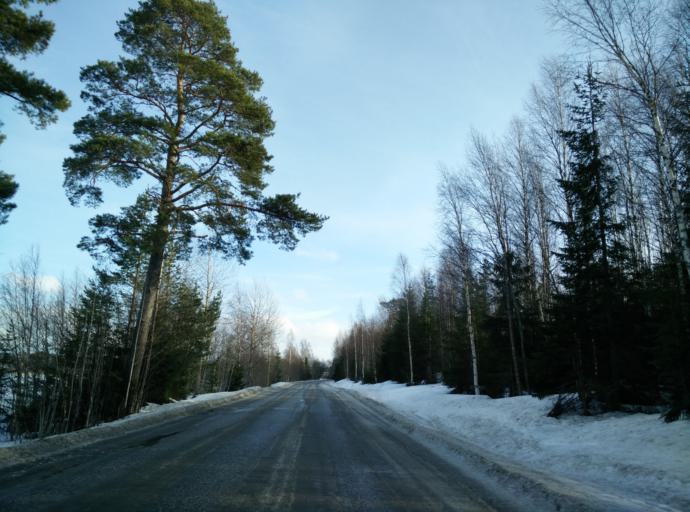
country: SE
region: Vaesternorrland
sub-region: Sundsvalls Kommun
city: Njurundabommen
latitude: 62.2218
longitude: 17.3290
